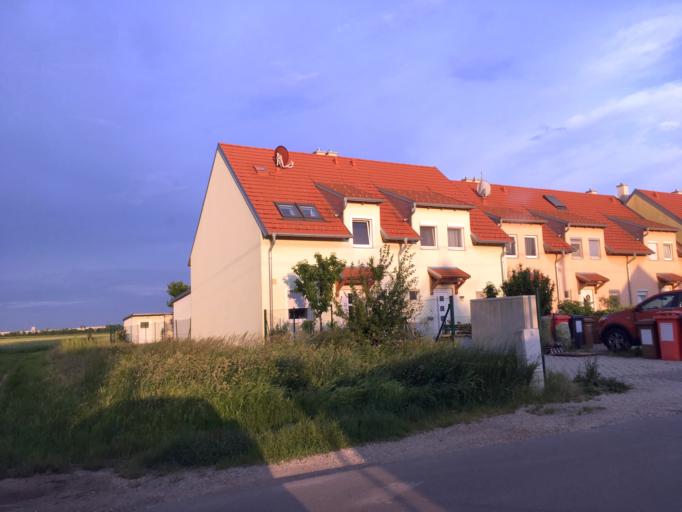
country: AT
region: Lower Austria
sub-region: Politischer Bezirk Wien-Umgebung
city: Gerasdorf bei Wien
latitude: 48.3127
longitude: 16.5014
